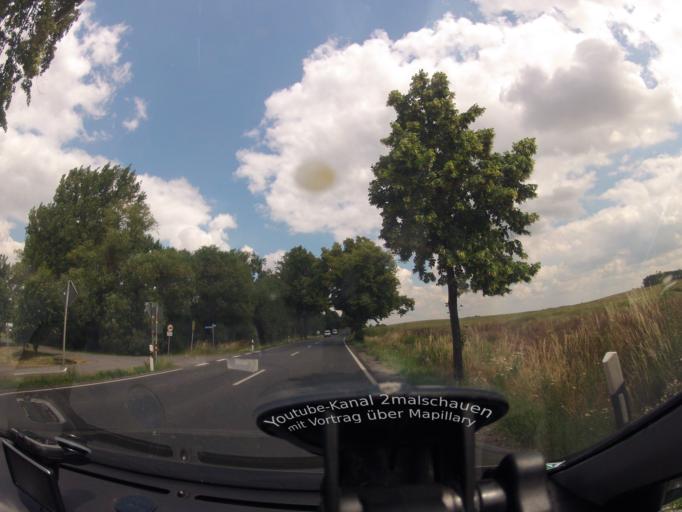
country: DE
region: Saxony
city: Jesewitz
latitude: 51.4088
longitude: 12.5393
